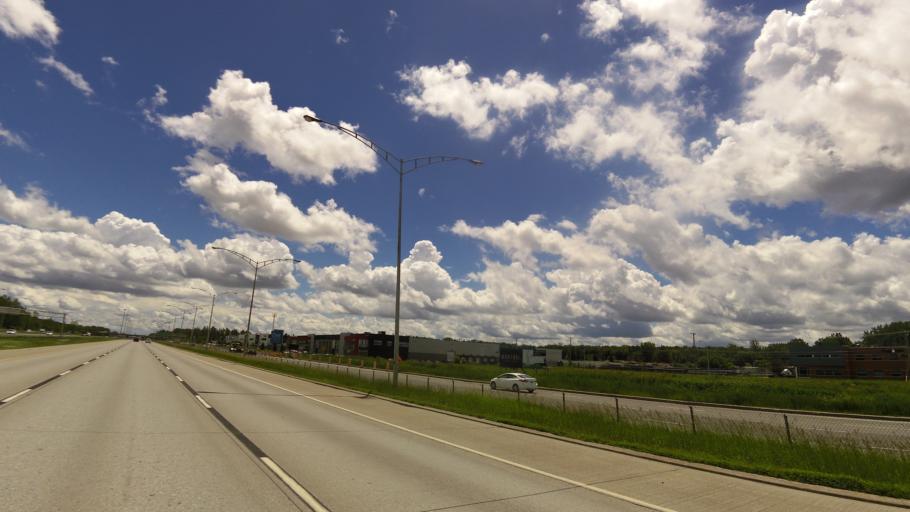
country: CA
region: Quebec
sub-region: Laurentides
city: Boisbriand
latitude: 45.5611
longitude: -73.8165
